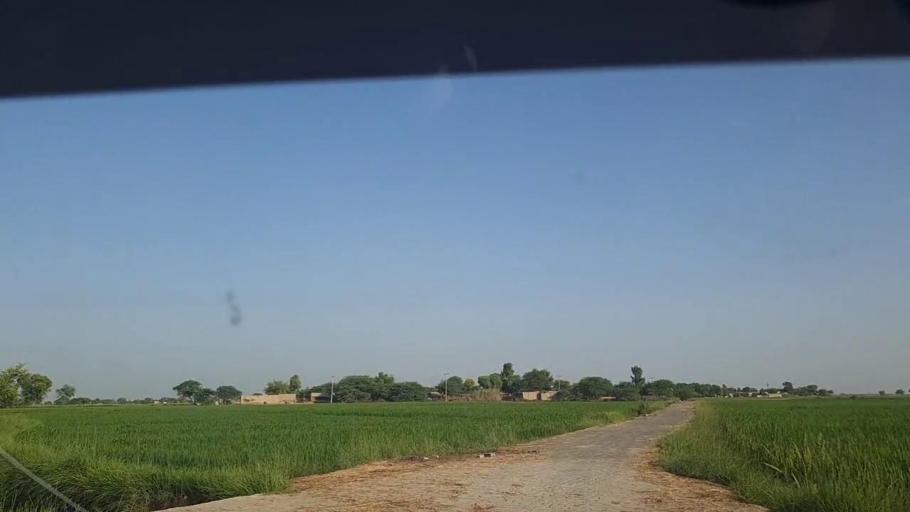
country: PK
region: Sindh
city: Tangwani
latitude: 28.2684
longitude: 69.0115
